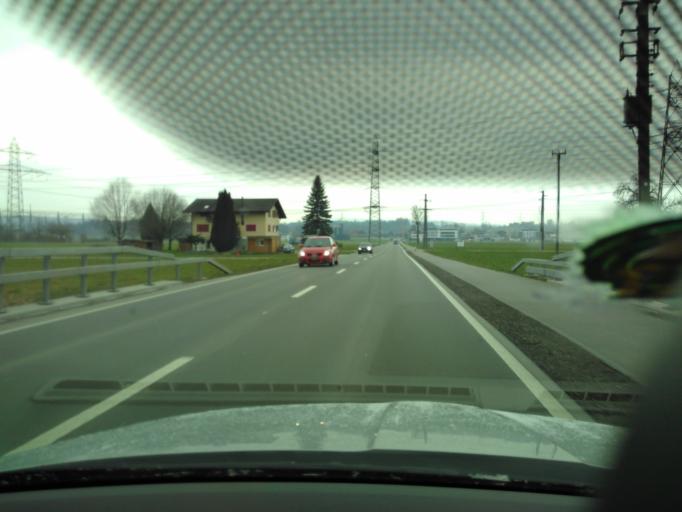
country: CH
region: Lucerne
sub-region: Hochdorf District
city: Inwil
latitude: 47.1138
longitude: 8.3423
